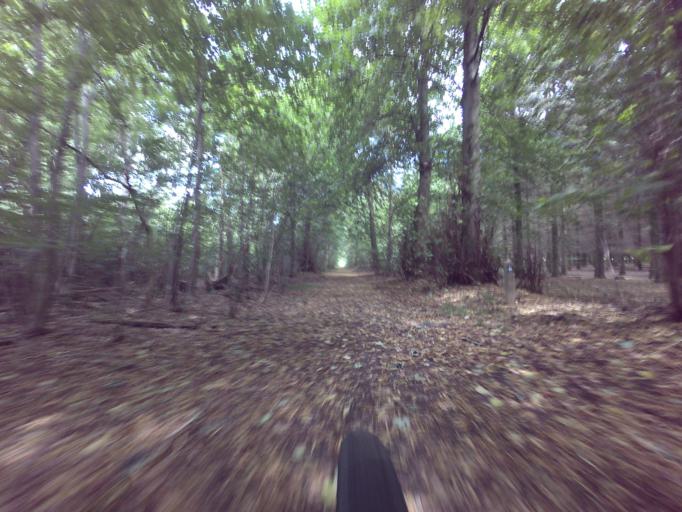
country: DK
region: Central Jutland
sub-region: Norddjurs Kommune
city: Allingabro
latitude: 56.4415
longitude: 10.3456
